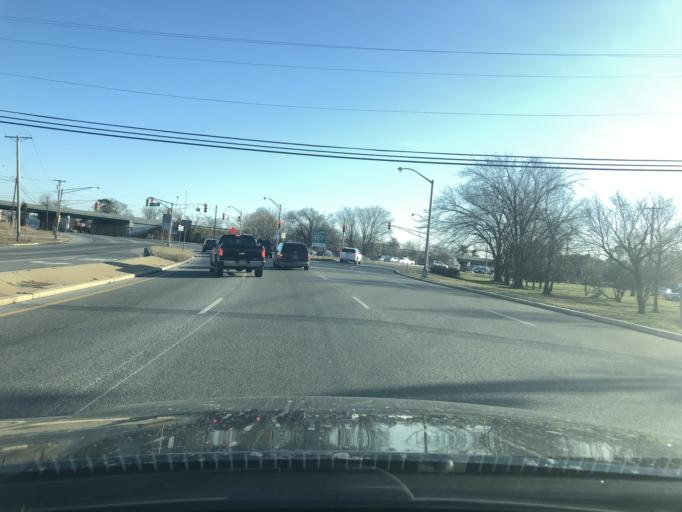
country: US
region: New Jersey
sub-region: Atlantic County
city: Northfield
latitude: 39.4012
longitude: -74.5618
